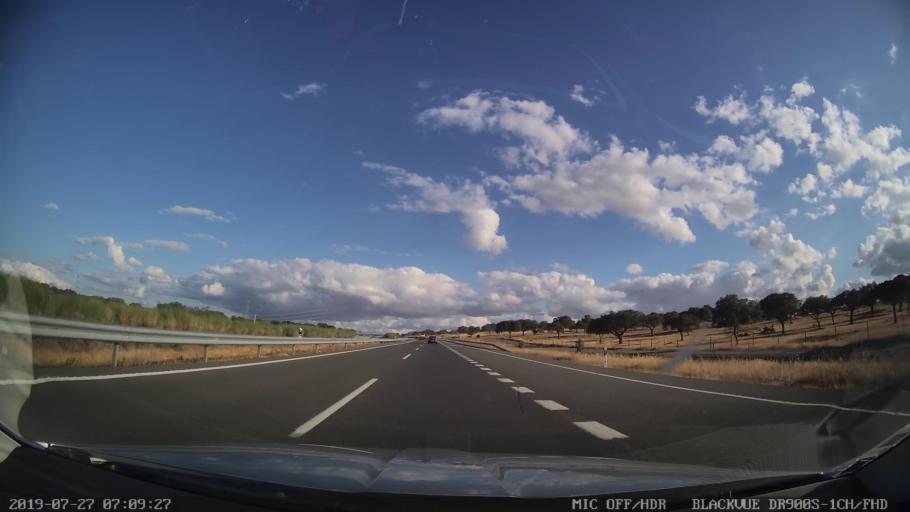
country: ES
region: Extremadura
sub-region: Provincia de Caceres
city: Jaraicejo
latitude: 39.5938
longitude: -5.8378
